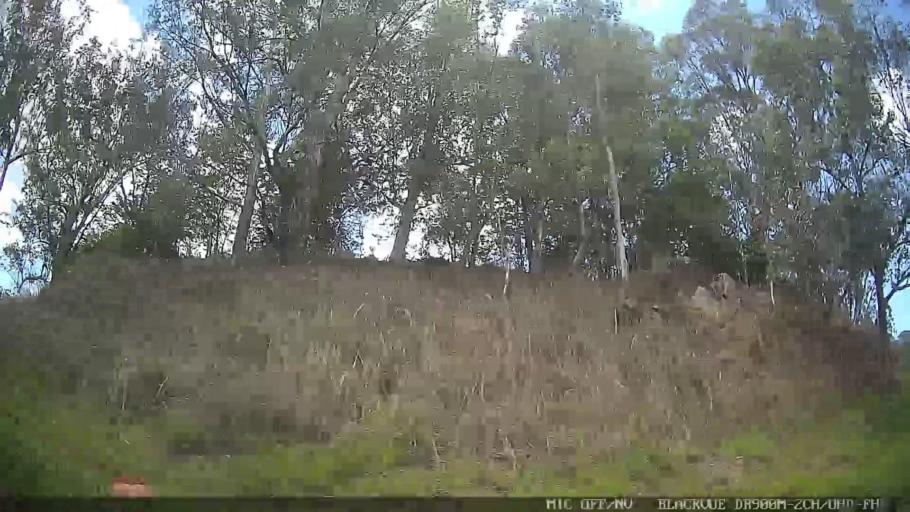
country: BR
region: Sao Paulo
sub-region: Serra Negra
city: Serra Negra
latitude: -22.6469
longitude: -46.7371
